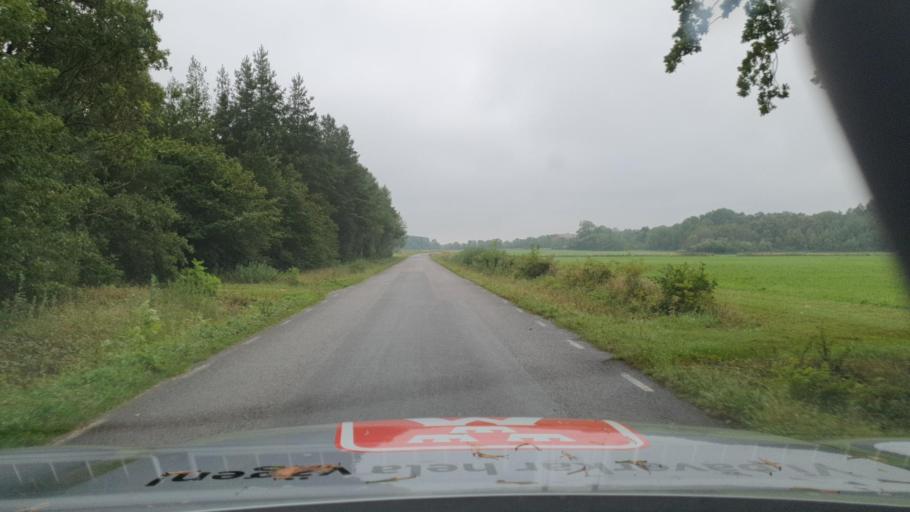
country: SE
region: Gotland
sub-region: Gotland
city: Visby
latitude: 57.7841
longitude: 18.5172
